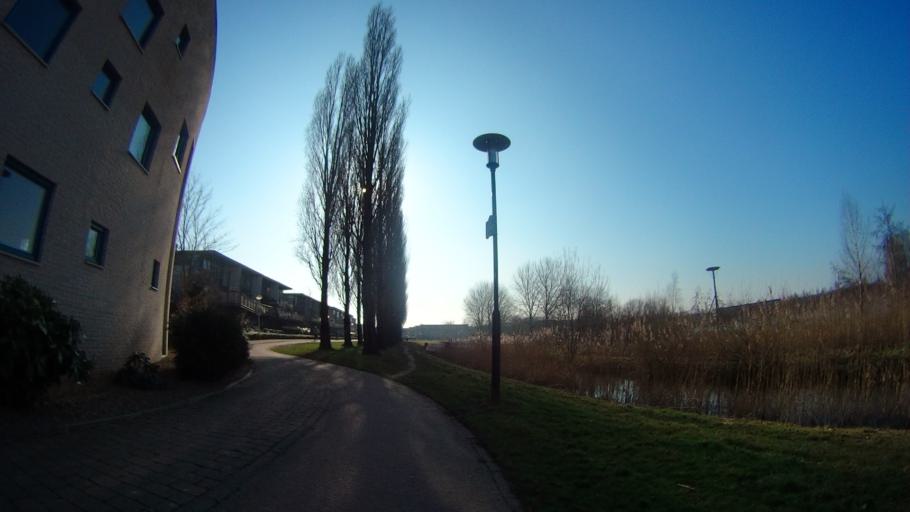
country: NL
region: Utrecht
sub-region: Gemeente Amersfoort
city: Hoogland
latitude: 52.1844
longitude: 5.3969
